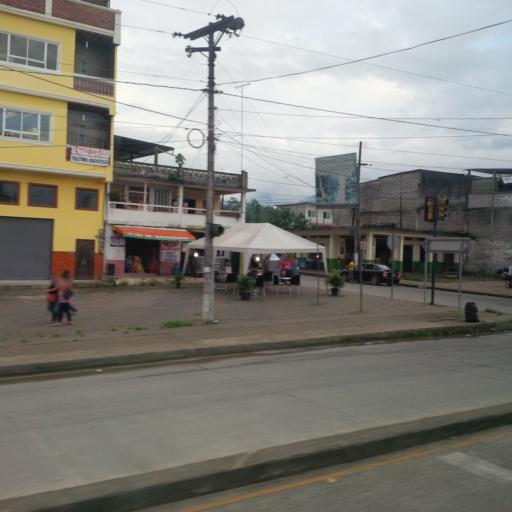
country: EC
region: Chimborazo
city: Alausi
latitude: -2.2075
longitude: -79.1342
